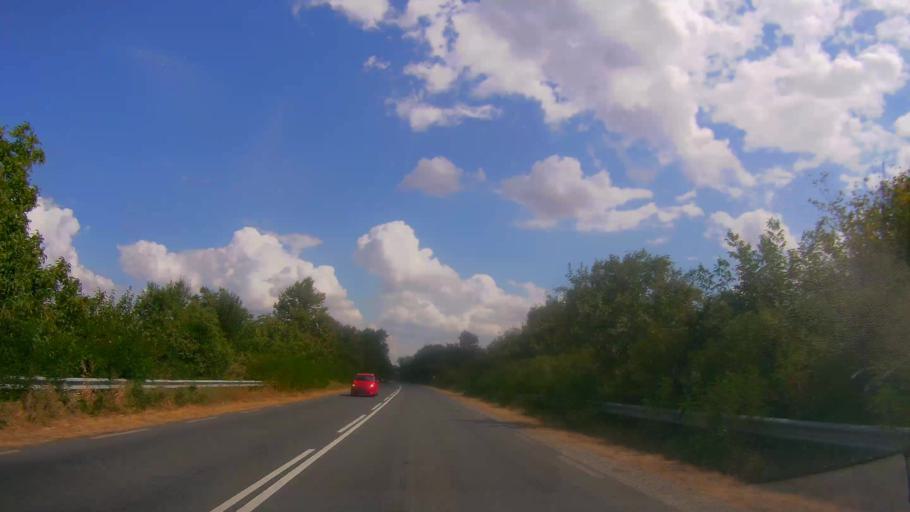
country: BG
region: Sliven
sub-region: Obshtina Sliven
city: Kermen
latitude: 42.6315
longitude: 26.1759
